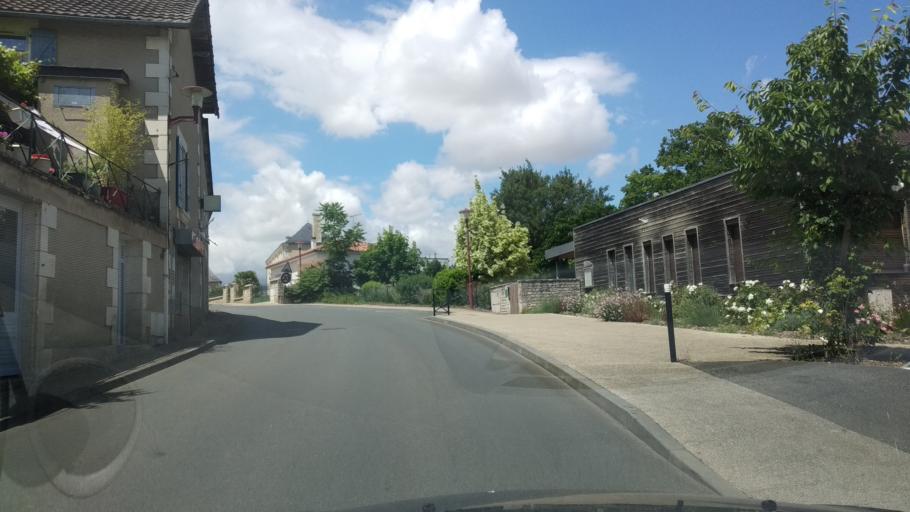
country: FR
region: Poitou-Charentes
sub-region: Departement de la Vienne
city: Cisse
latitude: 46.6070
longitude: 0.2365
